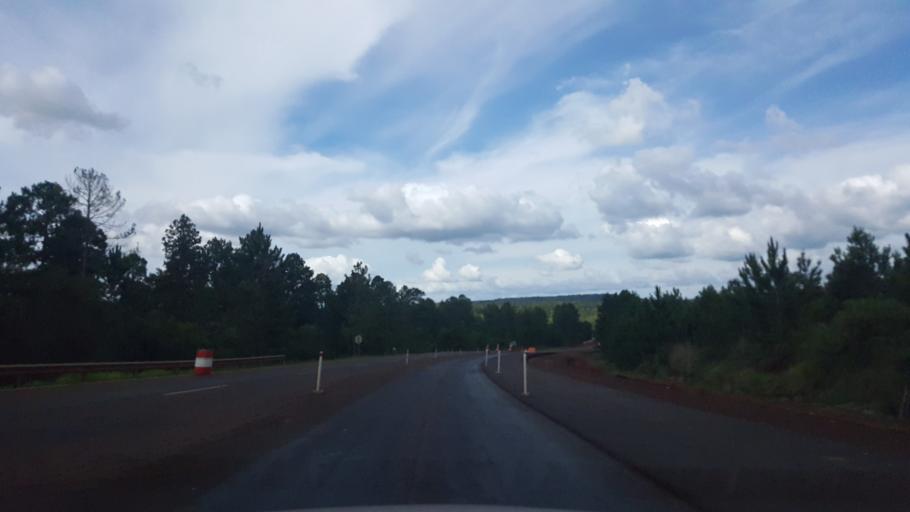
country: AR
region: Misiones
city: Santa Ana
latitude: -27.3905
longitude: -55.5979
